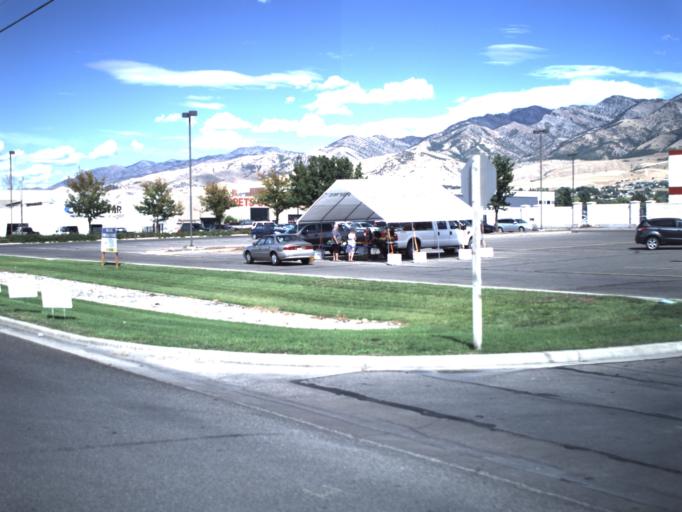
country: US
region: Utah
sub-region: Cache County
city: Hyde Park
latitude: 41.7734
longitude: -111.8340
